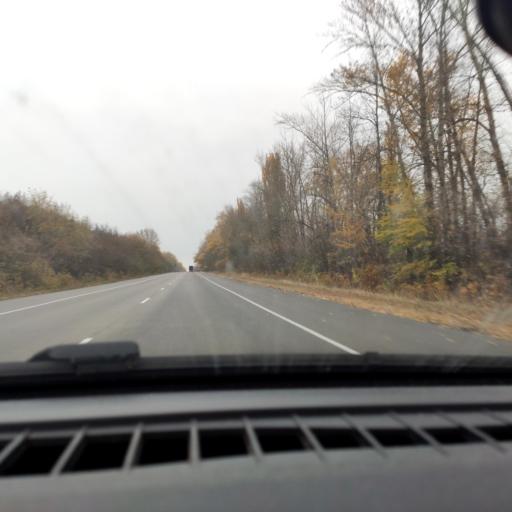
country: RU
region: Voronezj
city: Uryv-Pokrovka
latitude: 51.1636
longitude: 39.0703
